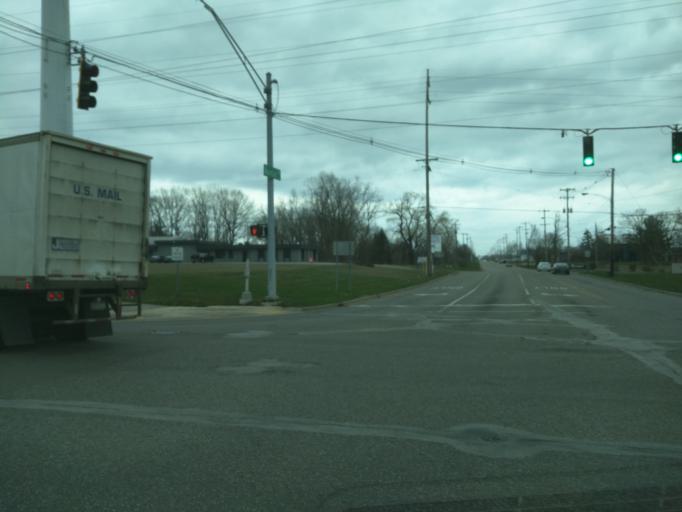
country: US
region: Michigan
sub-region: Ingham County
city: Holt
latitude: 42.6829
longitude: -84.5234
